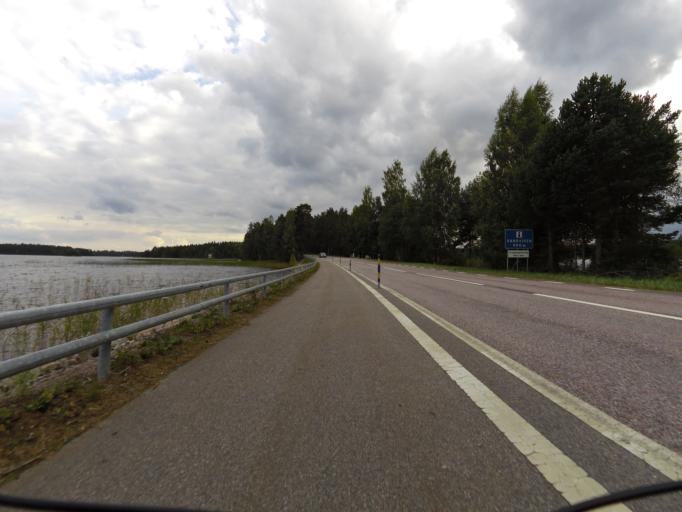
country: SE
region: Gaevleborg
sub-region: Sandvikens Kommun
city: Sandviken
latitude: 60.6976
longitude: 16.8169
